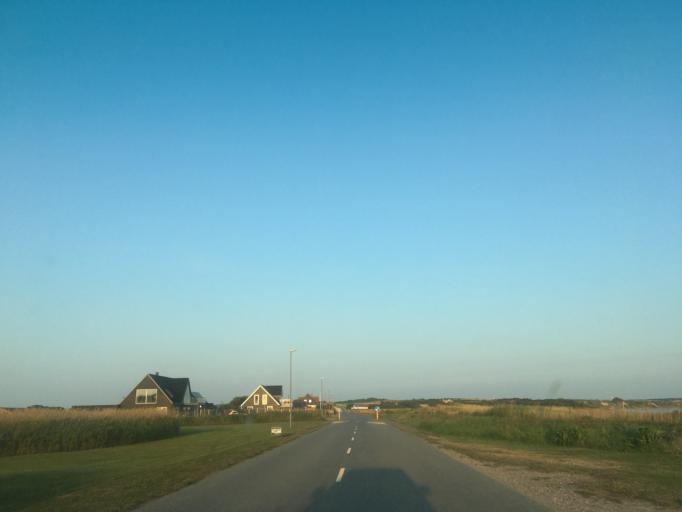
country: DK
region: Central Jutland
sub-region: Lemvig Kommune
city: Thyboron
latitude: 56.7701
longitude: 8.2807
